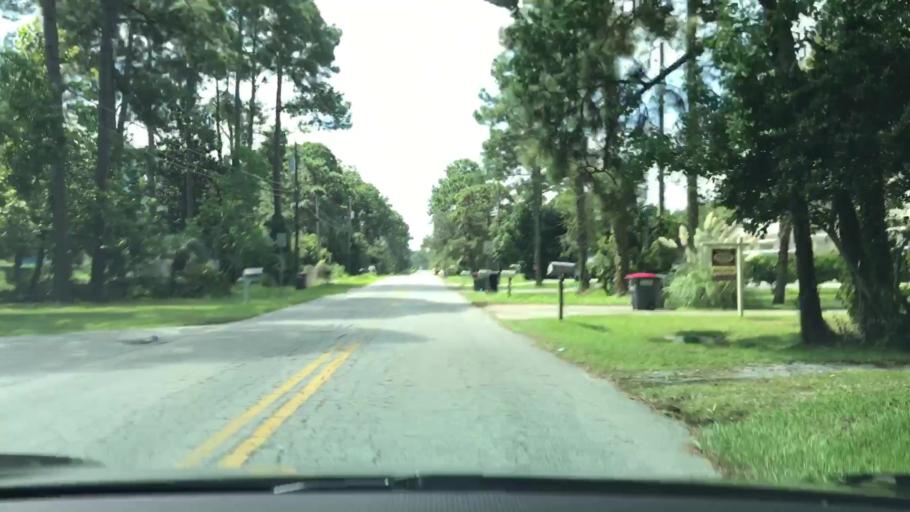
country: US
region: Florida
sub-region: Bay County
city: Panama City Beach
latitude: 30.1768
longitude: -85.7866
